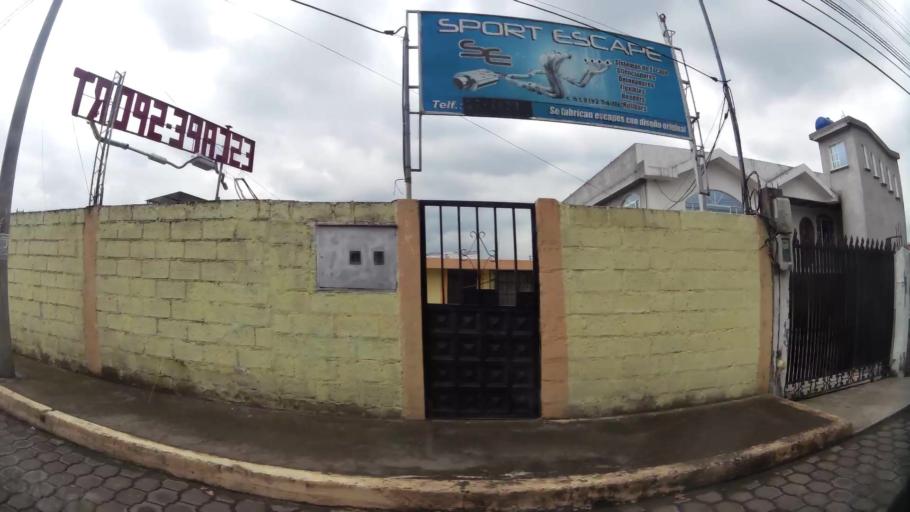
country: EC
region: Pichincha
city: Sangolqui
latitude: -0.3284
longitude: -78.4747
